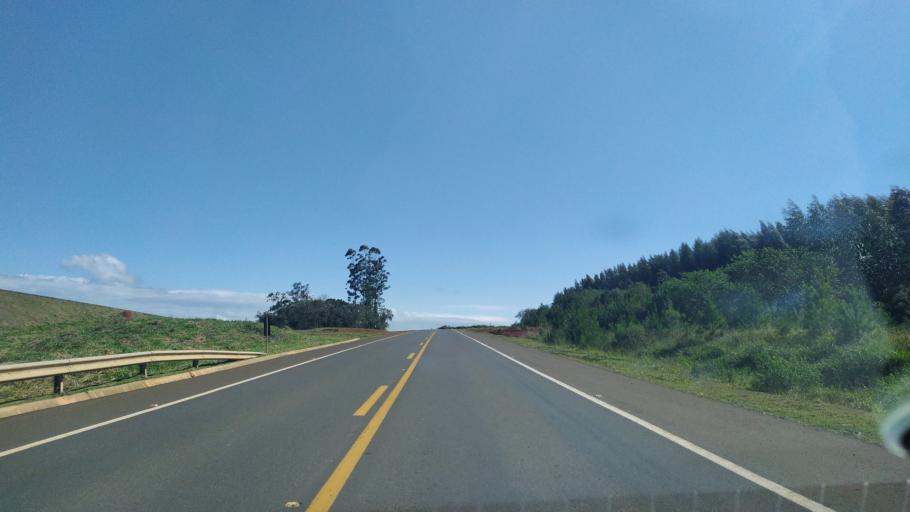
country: BR
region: Parana
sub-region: Ortigueira
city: Ortigueira
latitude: -24.2558
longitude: -50.8002
